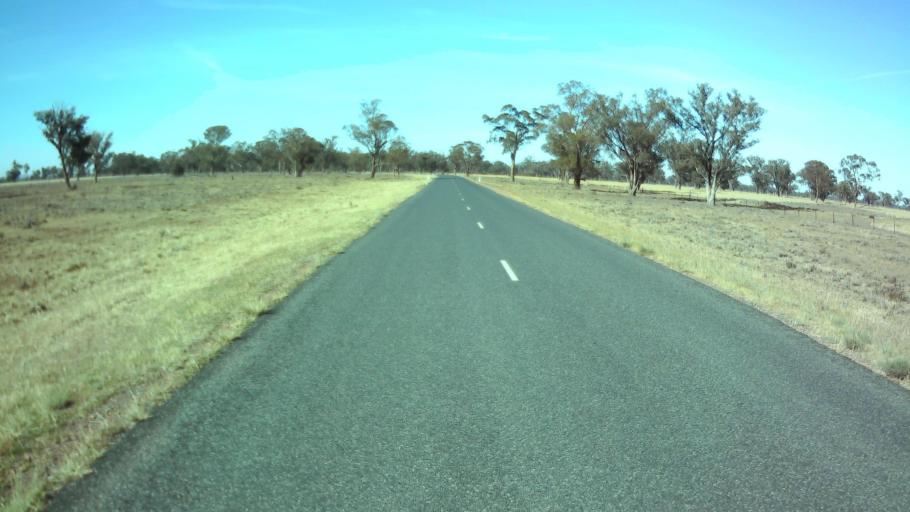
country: AU
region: New South Wales
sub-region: Weddin
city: Grenfell
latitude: -34.0567
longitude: 147.9134
